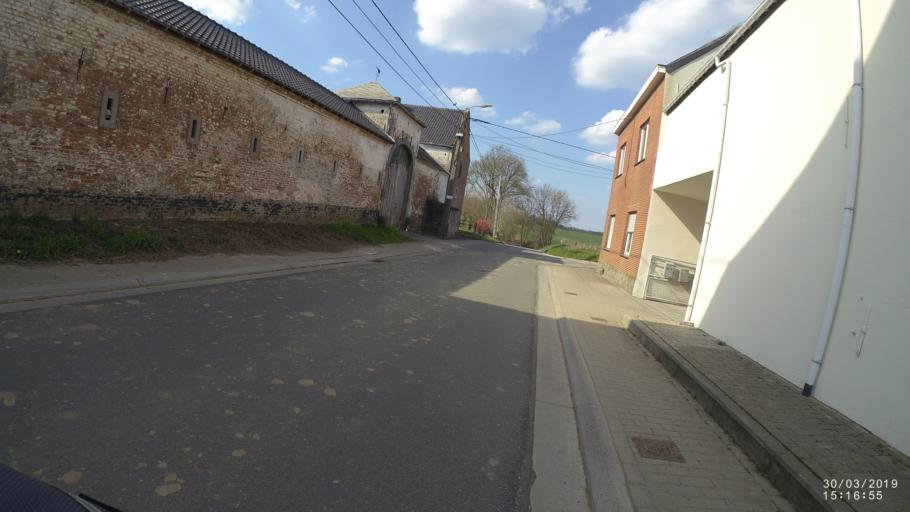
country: BE
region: Flanders
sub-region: Provincie Vlaams-Brabant
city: Overijse
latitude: 50.7548
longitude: 4.5401
